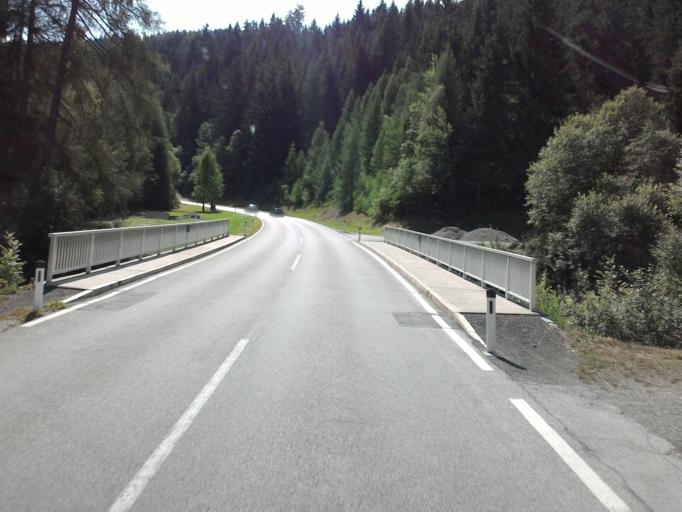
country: AT
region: Tyrol
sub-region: Politischer Bezirk Lienz
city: Heinfels
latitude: 46.7437
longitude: 12.4677
